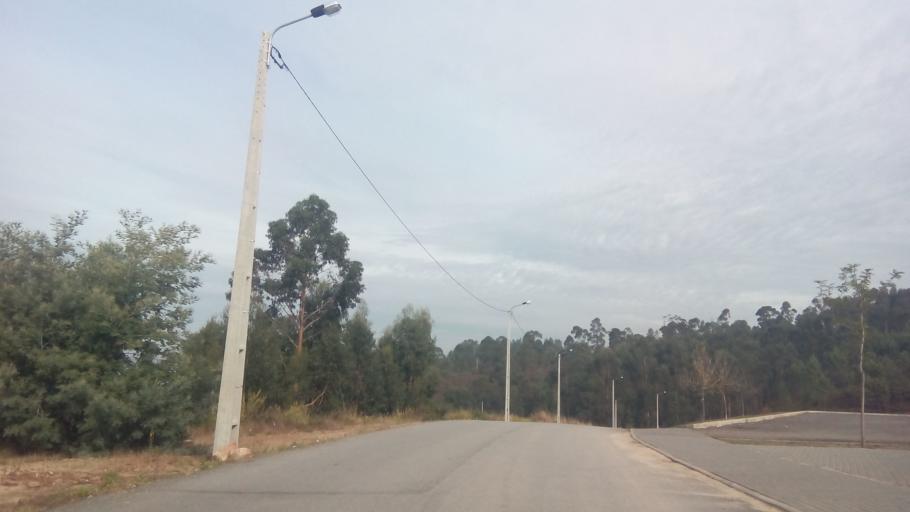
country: PT
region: Porto
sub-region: Paredes
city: Gandra
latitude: 41.1875
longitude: -8.4178
